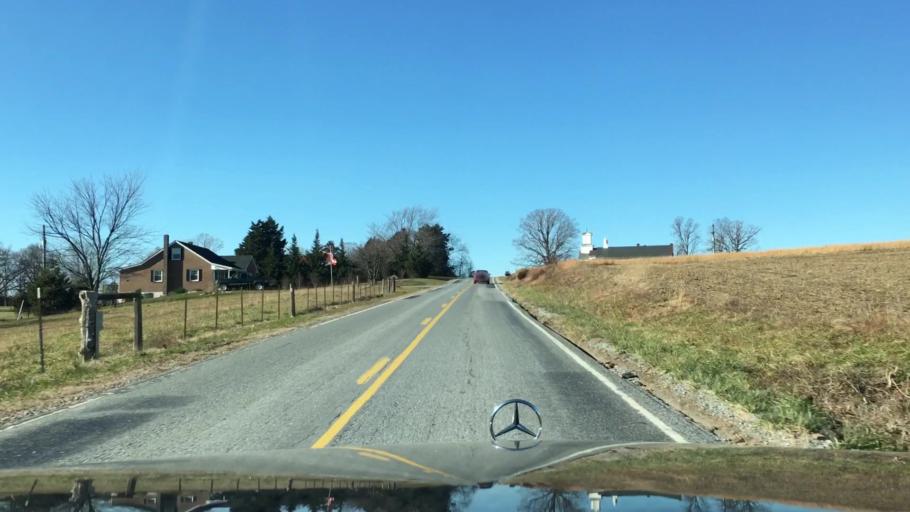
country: US
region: Virginia
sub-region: Pittsylvania County
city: Motley
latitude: 37.1910
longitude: -79.4245
